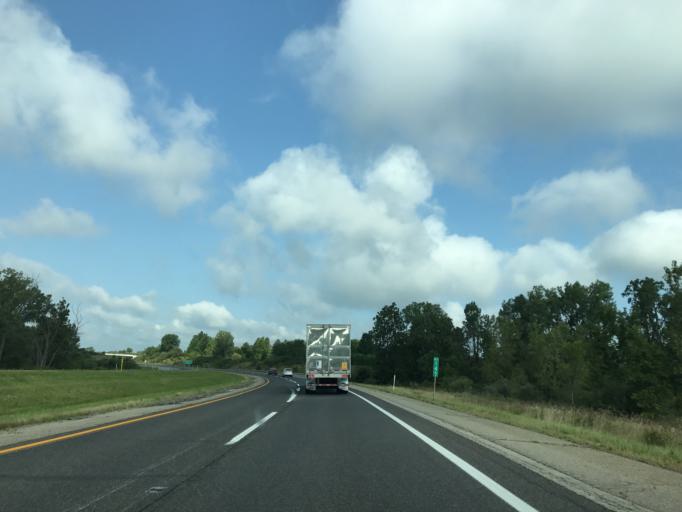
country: US
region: Indiana
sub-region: Steuben County
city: Fremont
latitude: 41.7340
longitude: -84.9745
